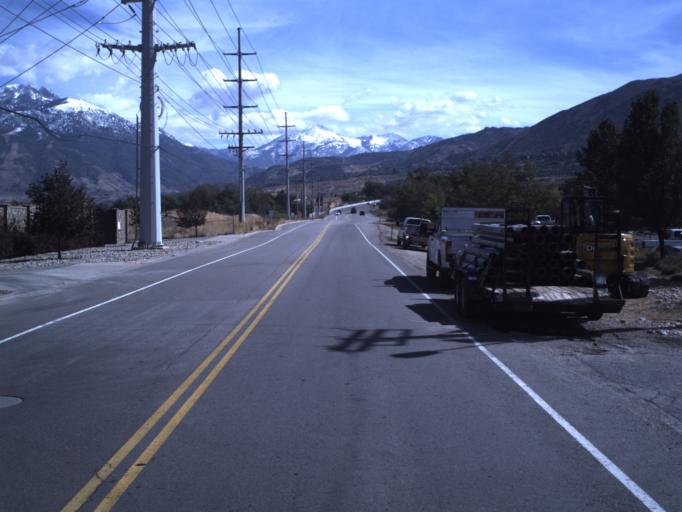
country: US
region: Utah
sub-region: Salt Lake County
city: Bluffdale
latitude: 40.4862
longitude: -111.9088
